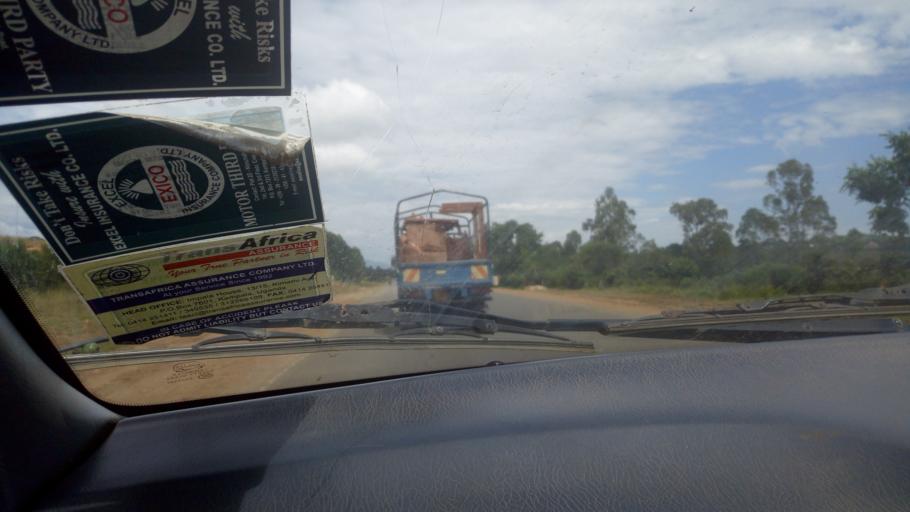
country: UG
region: Western Region
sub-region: Mbarara District
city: Bwizibwera
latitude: -0.4219
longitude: 30.5705
